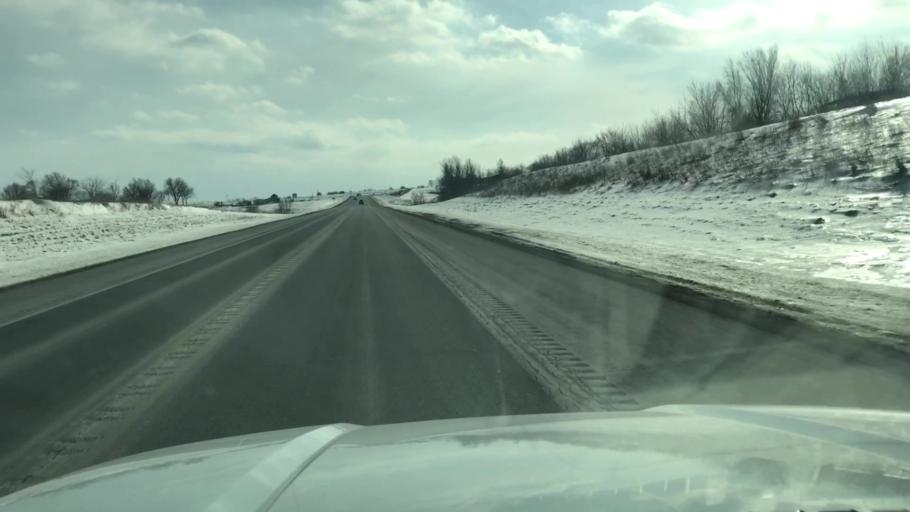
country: US
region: Missouri
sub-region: Nodaway County
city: Maryville
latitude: 40.3414
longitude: -94.8530
